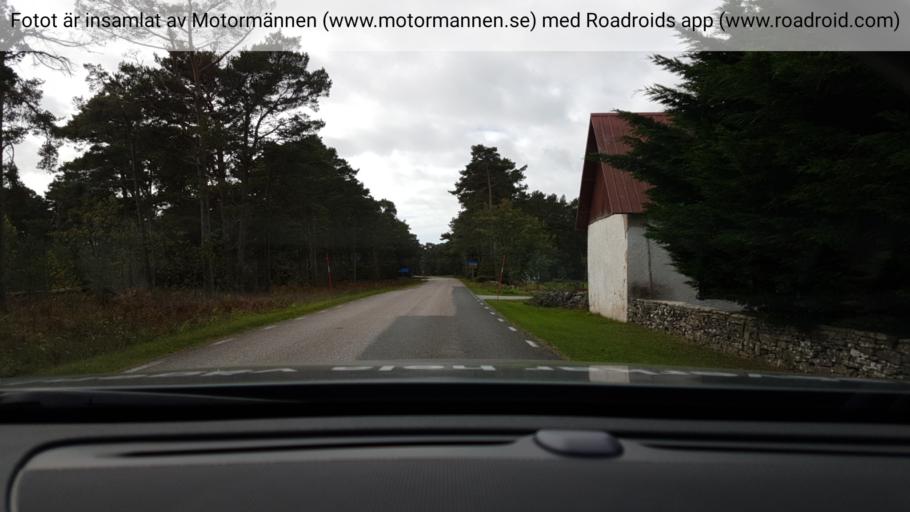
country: SE
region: Gotland
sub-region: Gotland
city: Hemse
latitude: 56.9542
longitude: 18.2123
